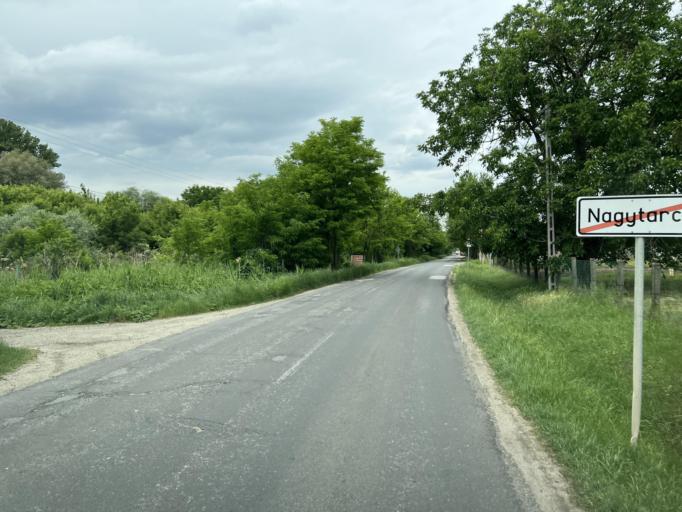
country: HU
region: Pest
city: Nagytarcsa
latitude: 47.5348
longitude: 19.2787
